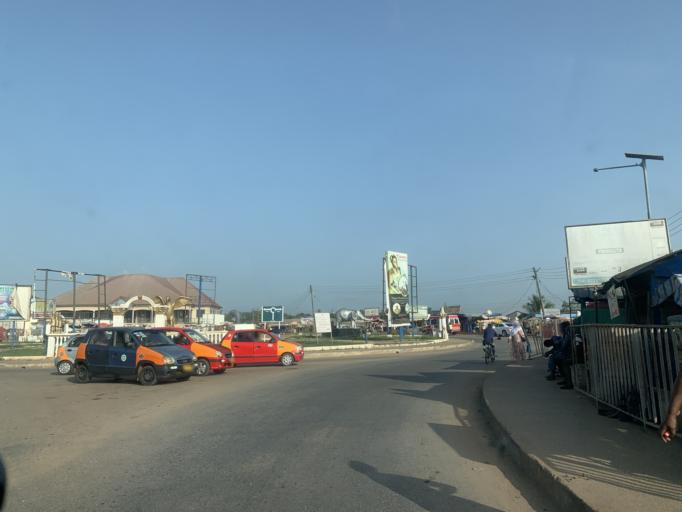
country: GH
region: Central
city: Saltpond
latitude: 5.2677
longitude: -1.0181
